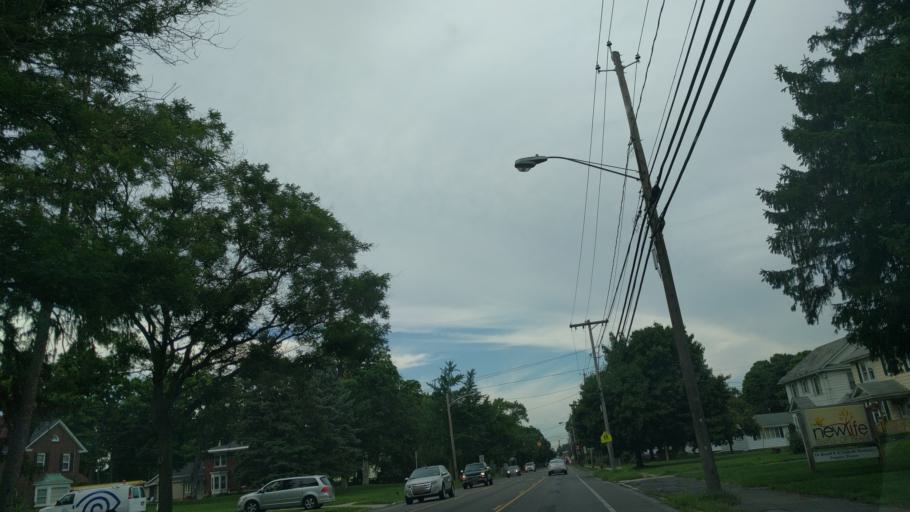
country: US
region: New York
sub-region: Onondaga County
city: Nedrow
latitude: 42.9953
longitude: -76.1434
